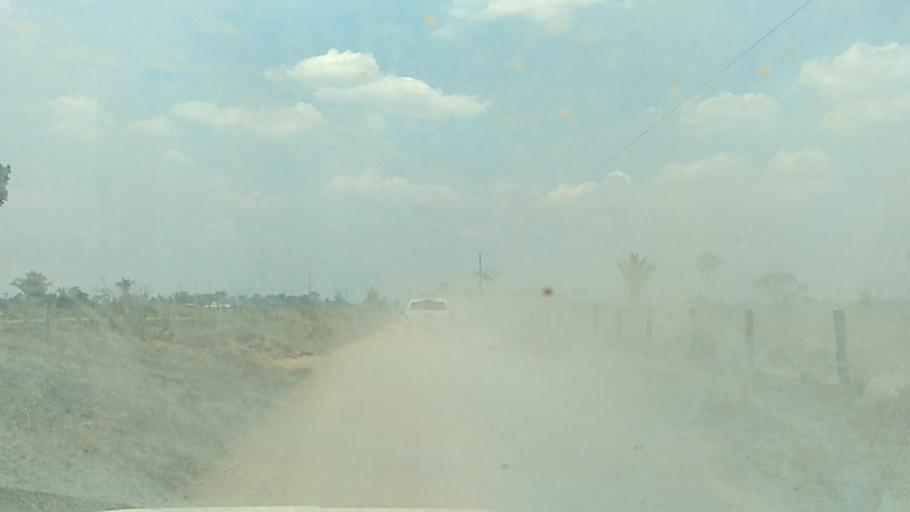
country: BR
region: Rondonia
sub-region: Porto Velho
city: Porto Velho
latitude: -8.7292
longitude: -63.2863
